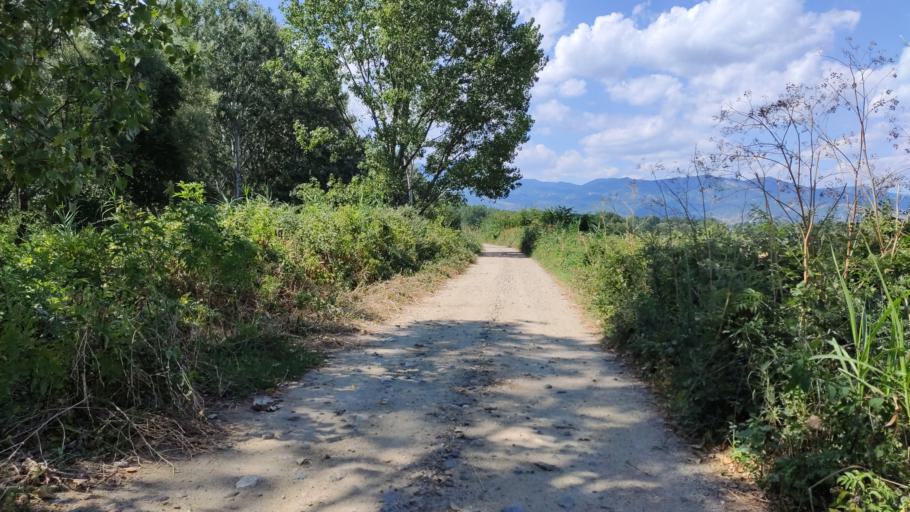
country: GR
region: East Macedonia and Thrace
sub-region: Nomos Rodopis
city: Komotini
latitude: 41.1122
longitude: 25.3708
